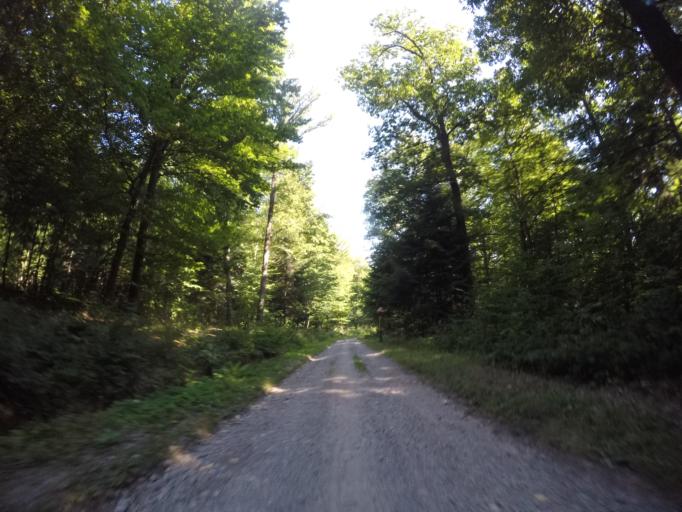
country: SK
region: Kosicky
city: Kosice
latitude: 48.7400
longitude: 21.1947
